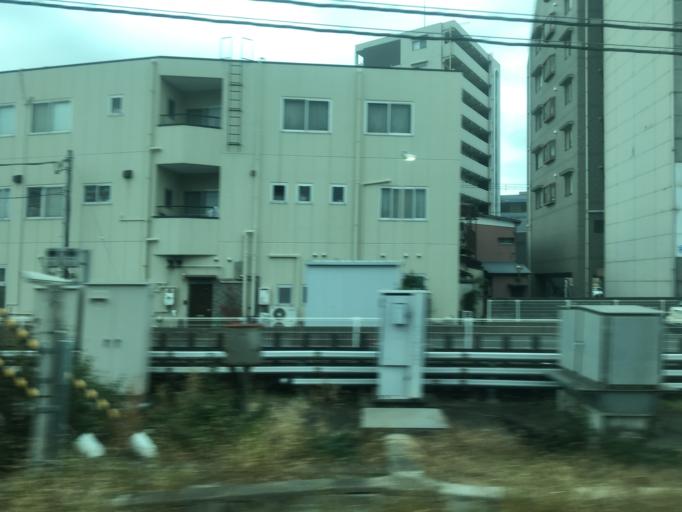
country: JP
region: Saitama
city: Okegawa
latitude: 35.9972
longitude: 139.5655
